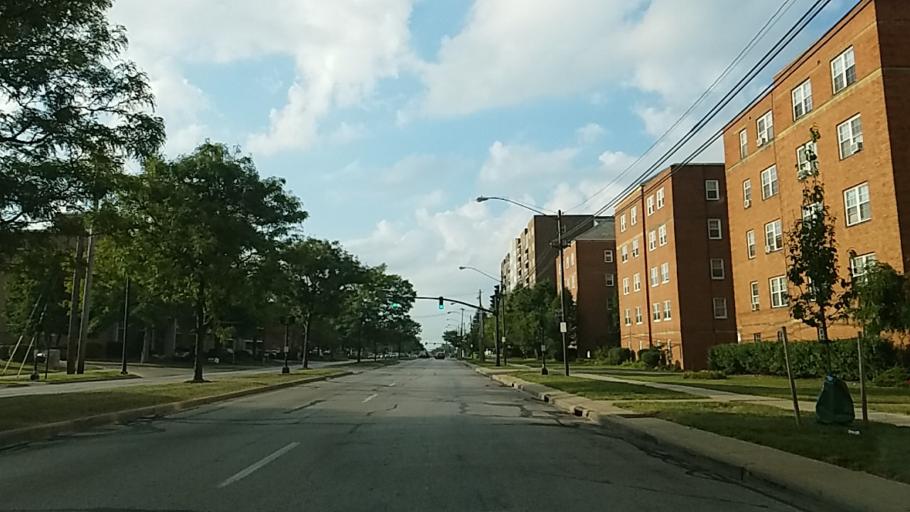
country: US
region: Ohio
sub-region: Cuyahoga County
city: Shaker Heights
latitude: 41.4705
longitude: -81.5364
